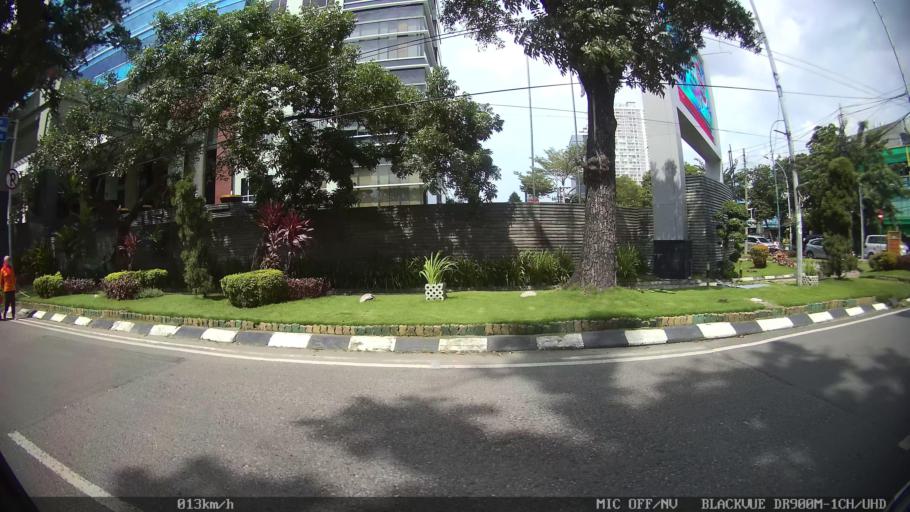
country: ID
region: North Sumatra
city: Medan
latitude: 3.5961
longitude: 98.6756
